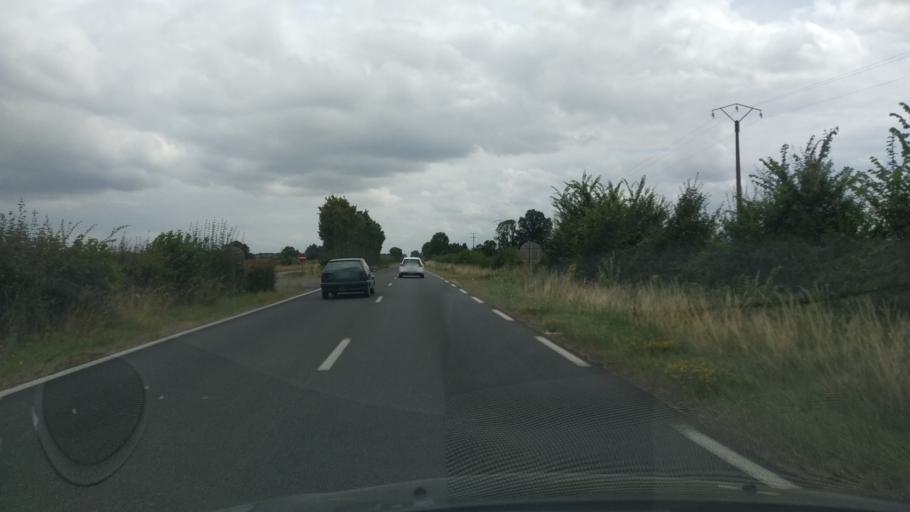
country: FR
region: Poitou-Charentes
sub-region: Departement de la Vienne
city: La Villedieu-du-Clain
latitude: 46.4191
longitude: 0.3832
